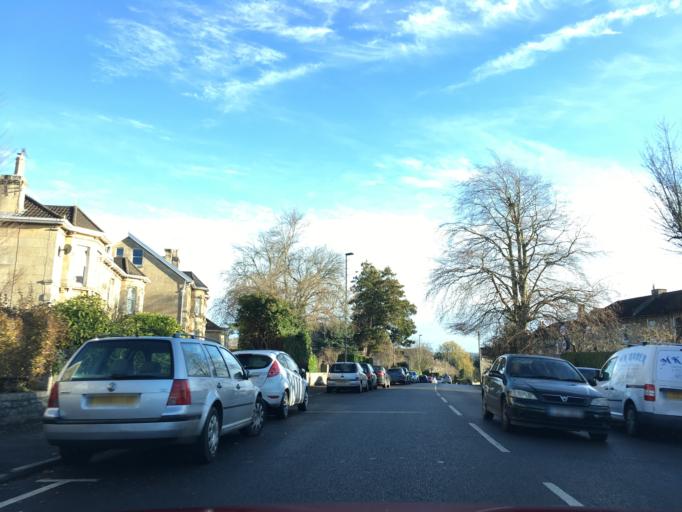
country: GB
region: England
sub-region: Bath and North East Somerset
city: Bath
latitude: 51.3877
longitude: -2.3933
